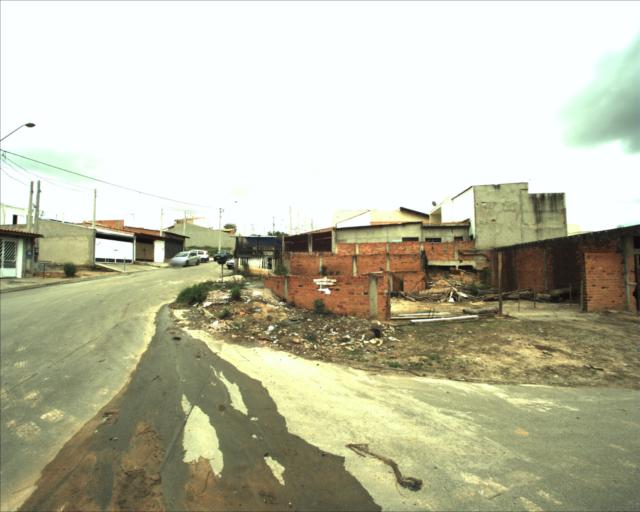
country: BR
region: Sao Paulo
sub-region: Sorocaba
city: Sorocaba
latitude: -23.4354
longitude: -47.4957
